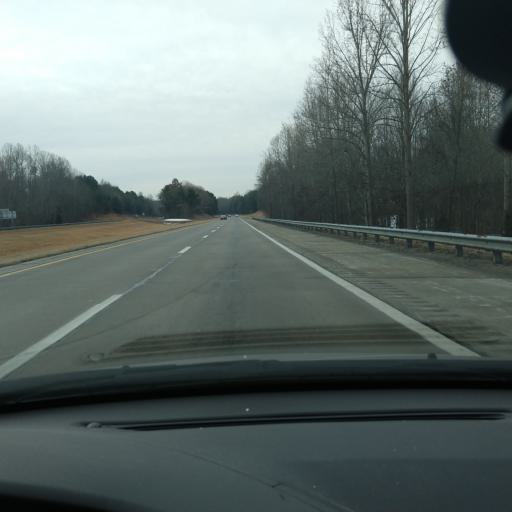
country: US
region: North Carolina
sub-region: Davidson County
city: Midway
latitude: 36.0000
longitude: -80.2376
